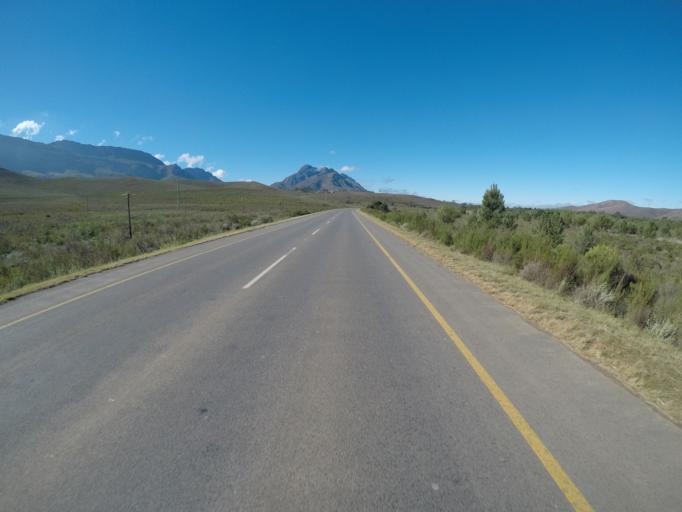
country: ZA
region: Western Cape
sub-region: Overberg District Municipality
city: Caledon
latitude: -34.0491
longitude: 19.5793
